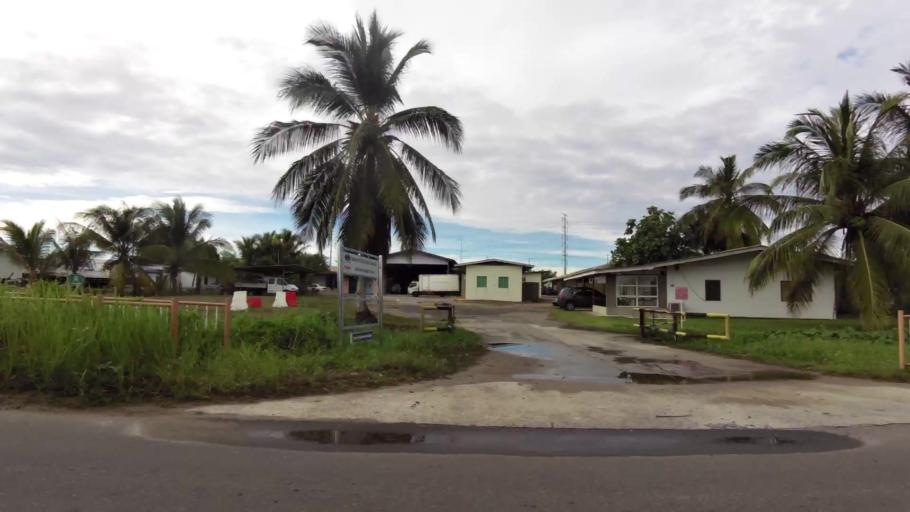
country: BN
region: Belait
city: Seria
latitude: 4.6140
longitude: 114.3529
